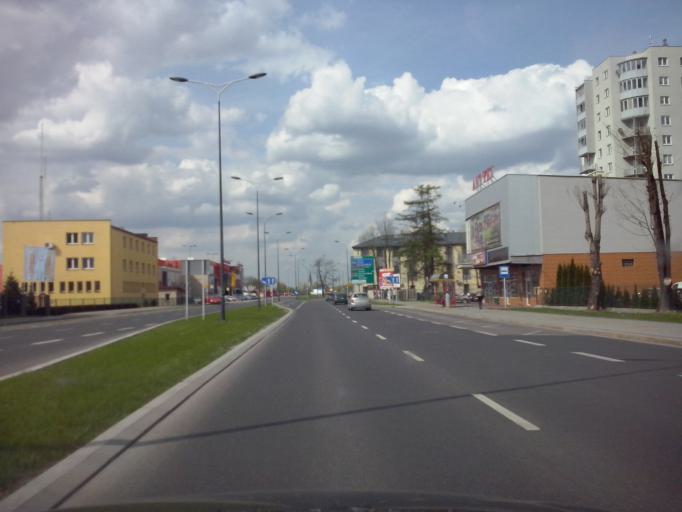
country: PL
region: Subcarpathian Voivodeship
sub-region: Rzeszow
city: Rzeszow
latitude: 50.0361
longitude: 22.0168
